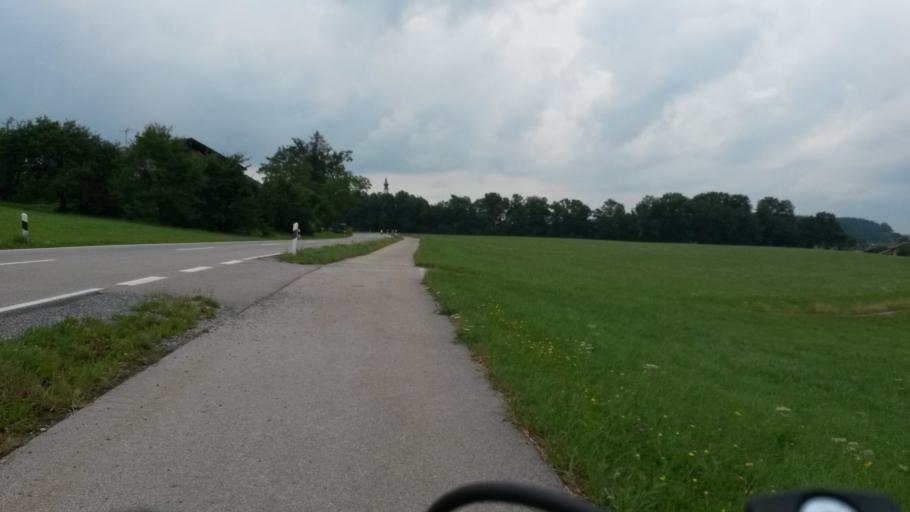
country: DE
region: Bavaria
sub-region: Upper Bavaria
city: Hoslwang
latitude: 47.9476
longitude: 12.3232
